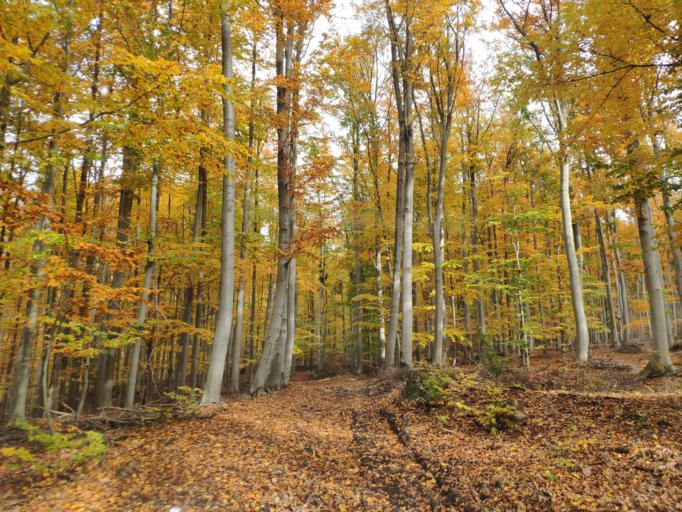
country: SK
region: Kosicky
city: Medzev
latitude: 48.7285
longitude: 20.9845
